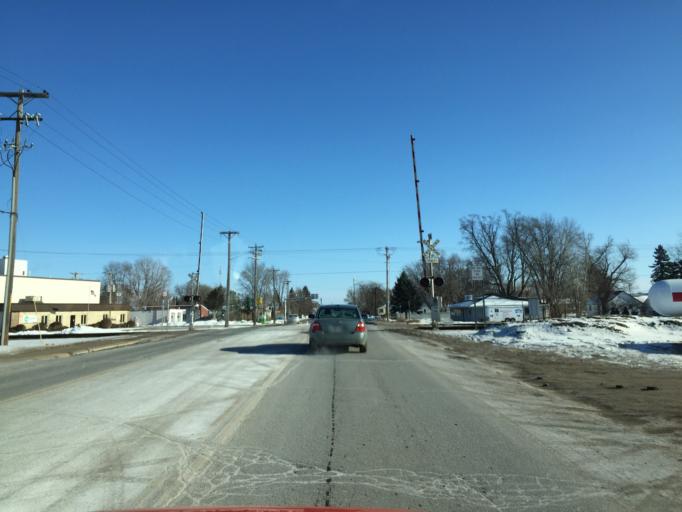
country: US
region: Minnesota
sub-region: Isanti County
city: Cambridge
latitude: 45.5727
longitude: -93.2211
